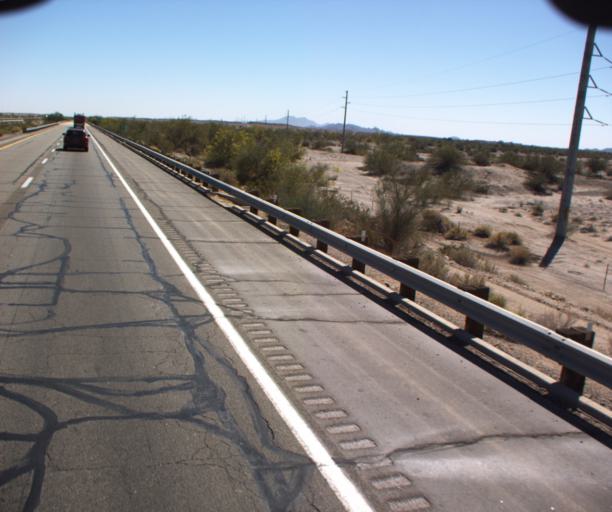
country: US
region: Arizona
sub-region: Yuma County
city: Wellton
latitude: 32.6601
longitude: -114.2559
